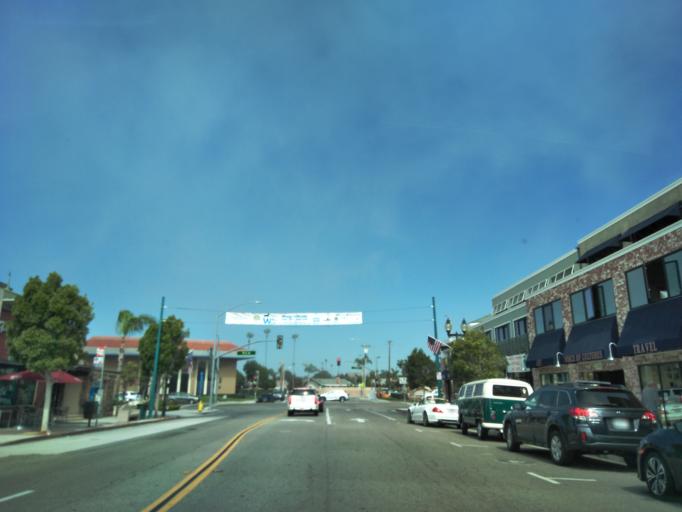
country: US
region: California
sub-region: Orange County
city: Seal Beach
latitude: 33.7439
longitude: -118.1029
